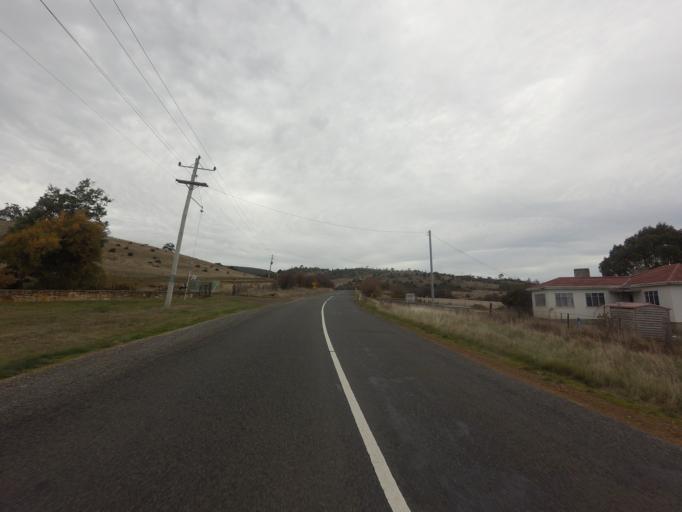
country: AU
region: Tasmania
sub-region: Derwent Valley
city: New Norfolk
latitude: -42.5301
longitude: 146.9394
